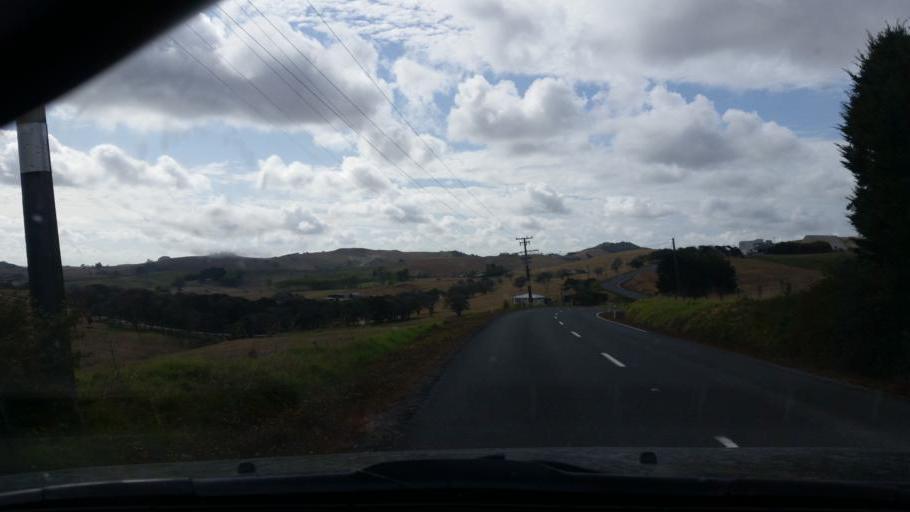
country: NZ
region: Northland
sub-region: Kaipara District
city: Dargaville
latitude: -35.9649
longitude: 173.9309
